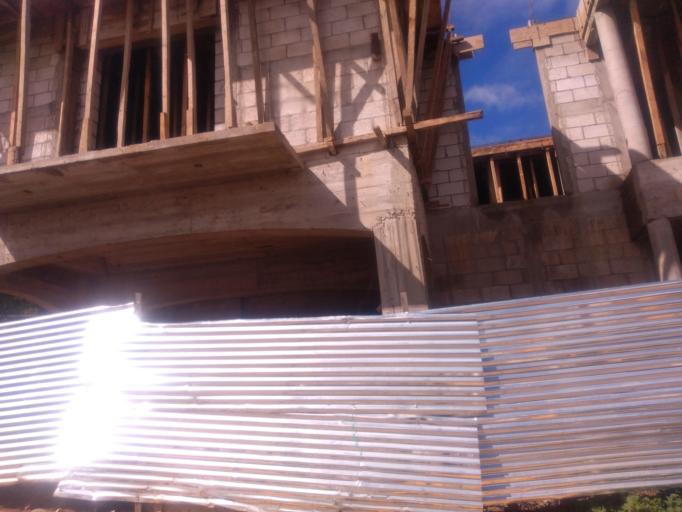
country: GT
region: Quetzaltenango
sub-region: Municipio de La Esperanza
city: La Esperanza
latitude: 14.8553
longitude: -91.5683
